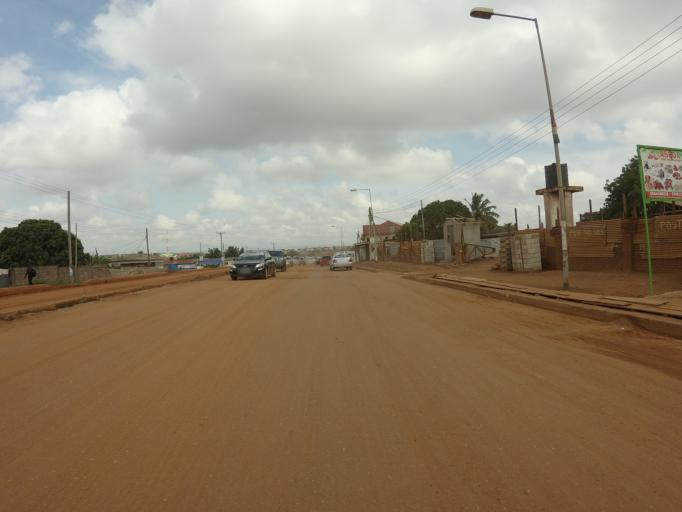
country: GH
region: Greater Accra
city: Teshi Old Town
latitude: 5.5976
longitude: -0.1185
